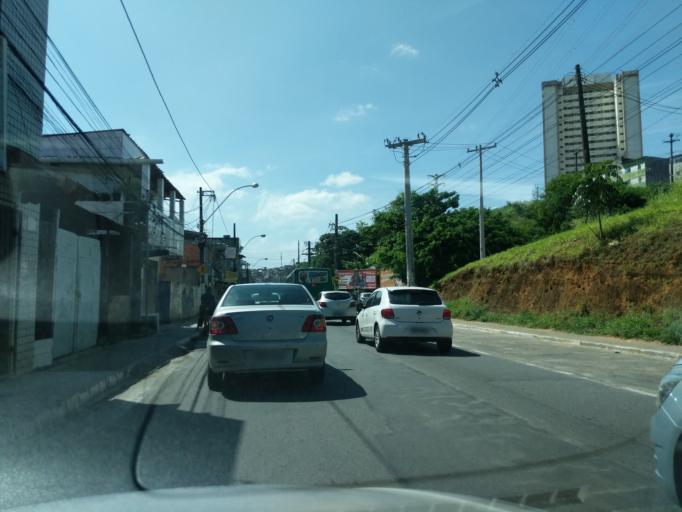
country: BR
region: Bahia
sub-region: Salvador
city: Salvador
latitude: -12.9555
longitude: -38.4428
